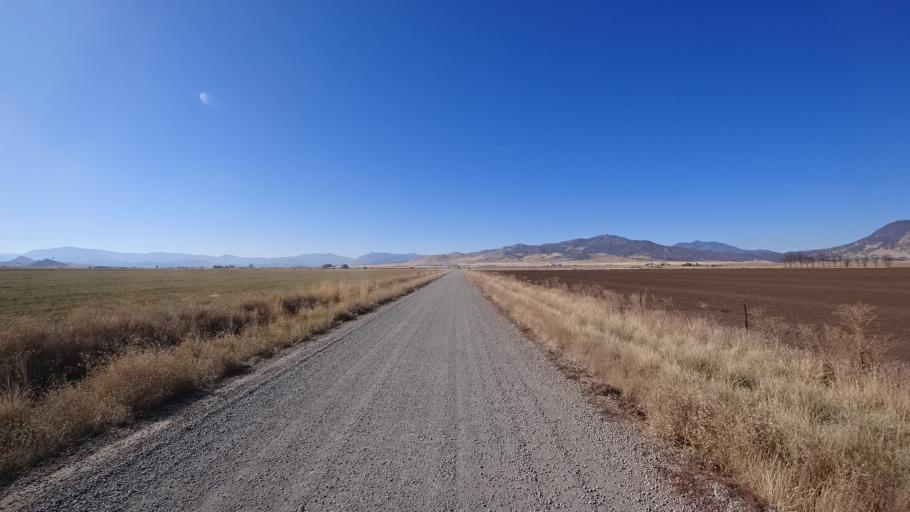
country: US
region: California
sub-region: Siskiyou County
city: Montague
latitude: 41.7864
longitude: -122.4568
